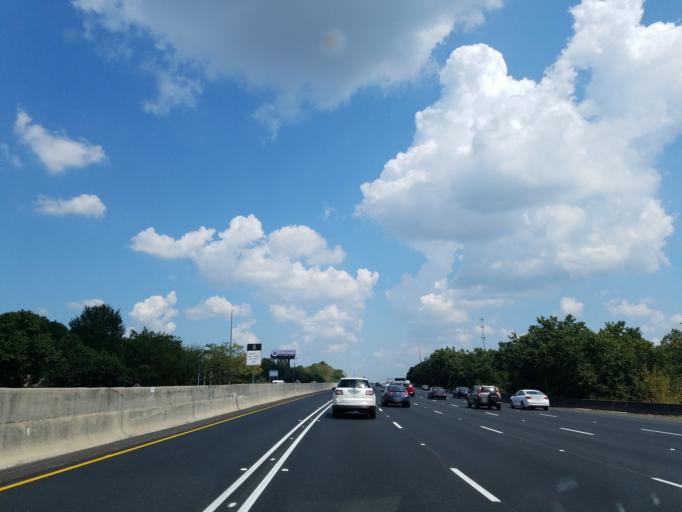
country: US
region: Georgia
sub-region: DeKalb County
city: Chamblee
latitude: 33.8682
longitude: -84.2846
